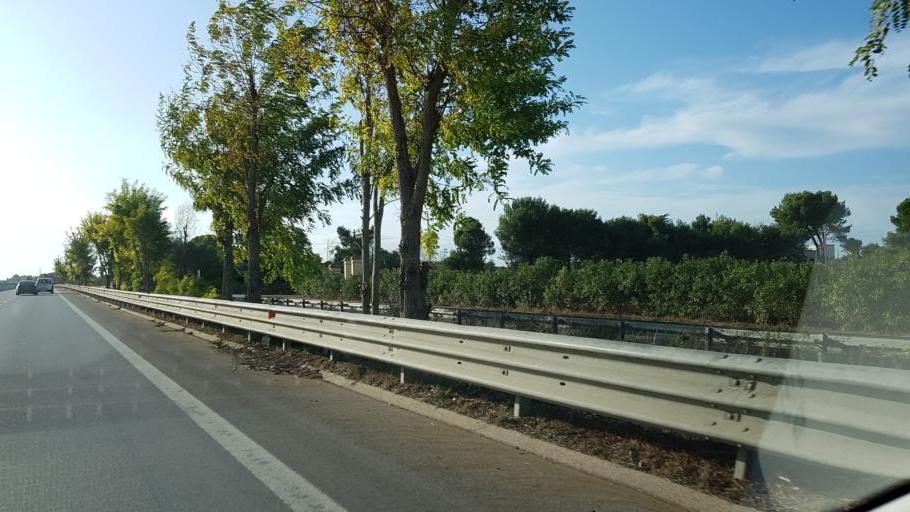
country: IT
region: Apulia
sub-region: Provincia di Brindisi
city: Oria
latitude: 40.5343
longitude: 17.6331
